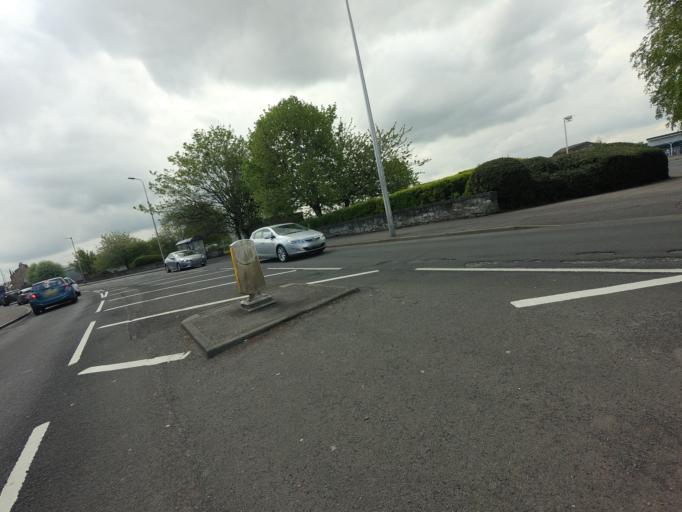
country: GB
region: Scotland
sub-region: Falkirk
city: Falkirk
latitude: 56.0163
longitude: -3.7916
